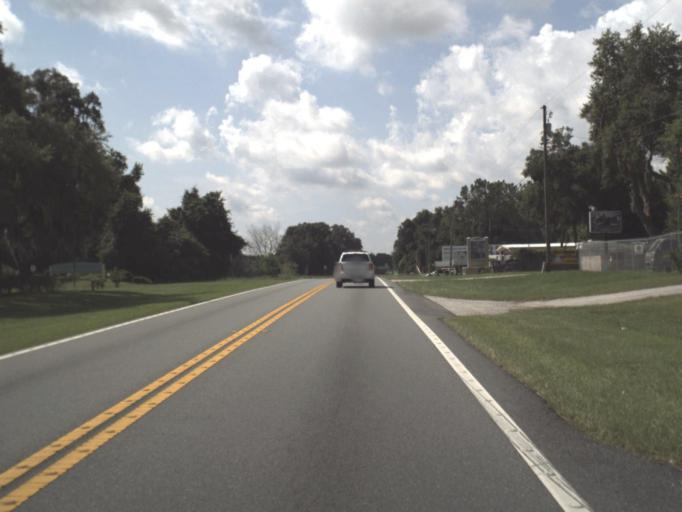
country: US
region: Florida
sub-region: Citrus County
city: Hernando
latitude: 28.8933
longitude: -82.3700
